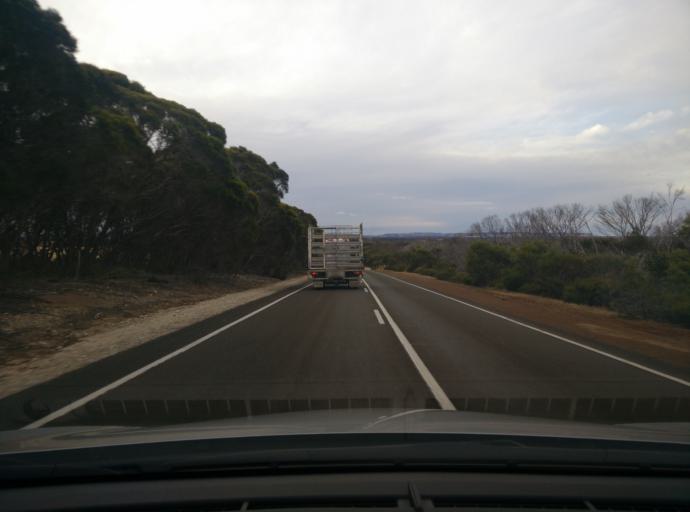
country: AU
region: South Australia
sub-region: Kangaroo Island
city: Kingscote
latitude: -35.7529
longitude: 137.5981
